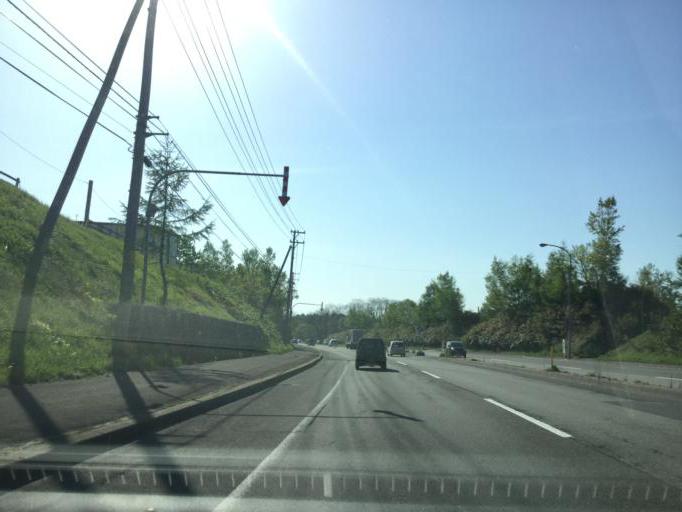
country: JP
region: Hokkaido
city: Kitahiroshima
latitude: 42.9998
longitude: 141.5363
